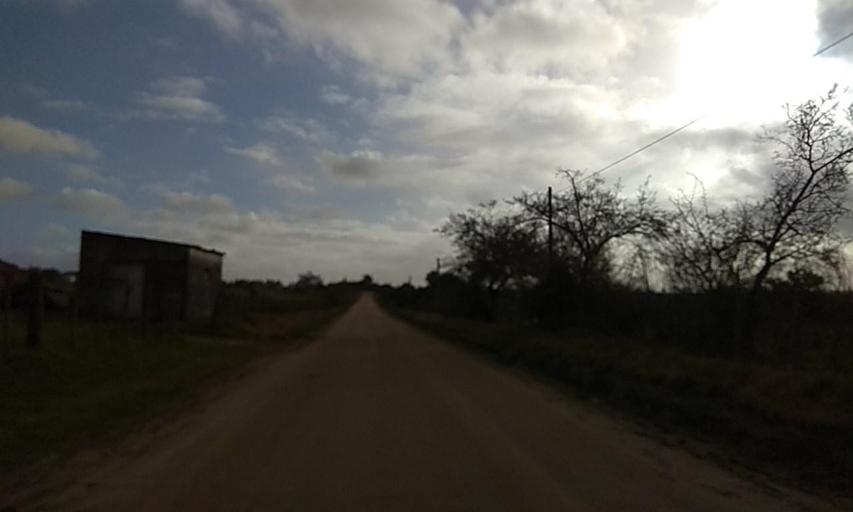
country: UY
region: Florida
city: Florida
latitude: -34.0586
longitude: -56.1914
